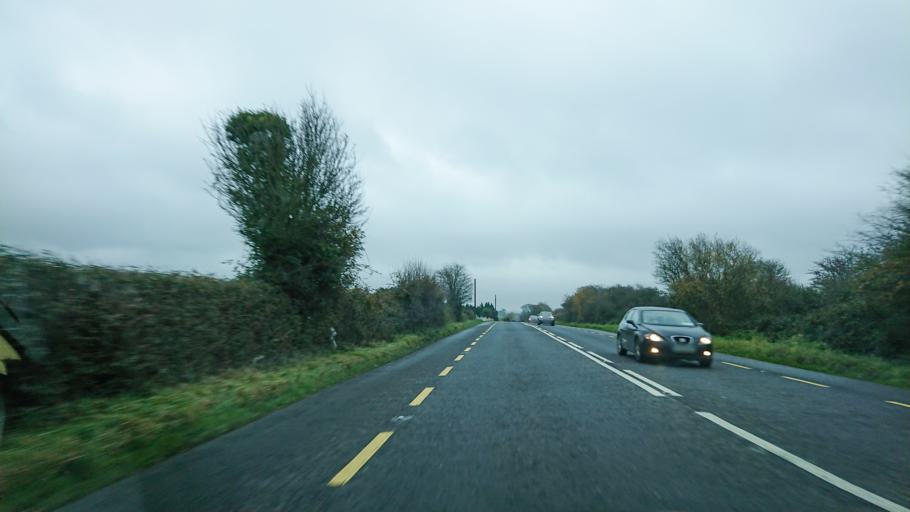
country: IE
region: Leinster
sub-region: Kilkenny
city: Mooncoin
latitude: 52.2873
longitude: -7.2216
